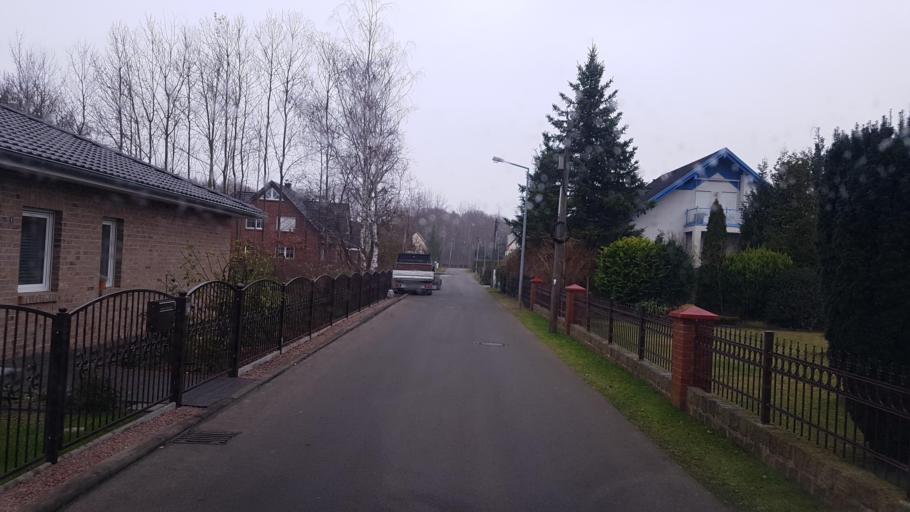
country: DE
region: Brandenburg
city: Lauchhammer
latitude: 51.4895
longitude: 13.7810
